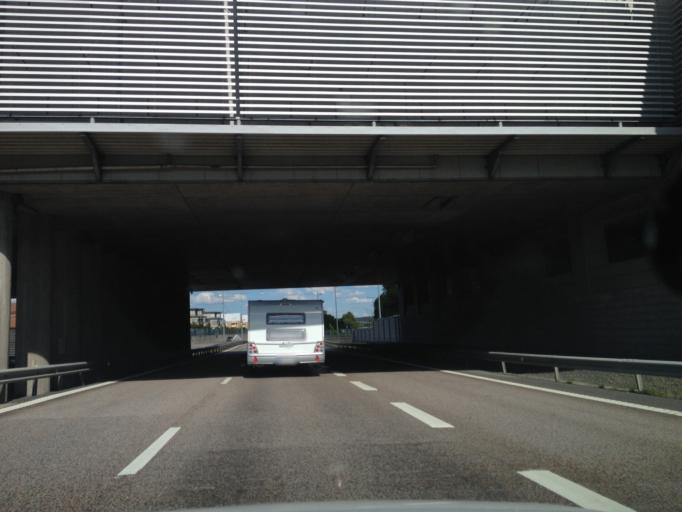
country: SE
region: Vaestra Goetaland
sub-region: Partille Kommun
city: Partille
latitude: 57.7379
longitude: 12.1048
